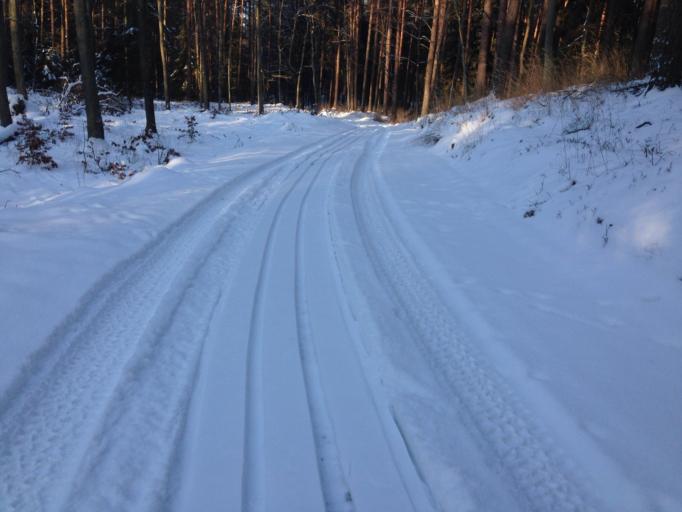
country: PL
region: Kujawsko-Pomorskie
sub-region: Powiat brodnicki
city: Gorzno
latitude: 53.1920
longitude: 19.6909
